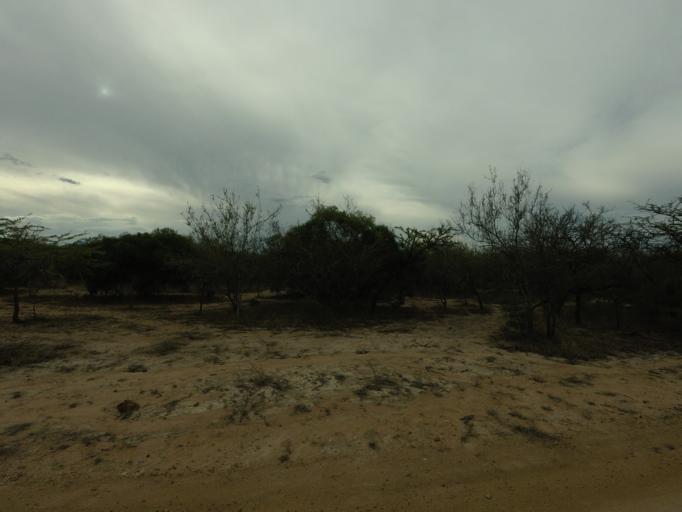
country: ZA
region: Limpopo
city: Thulamahashi
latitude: -24.5282
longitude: 31.1122
